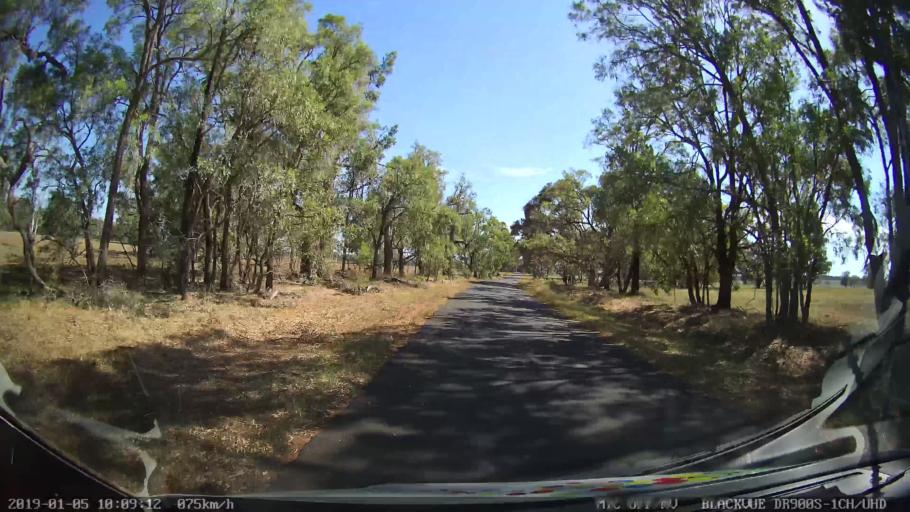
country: AU
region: New South Wales
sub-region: Gilgandra
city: Gilgandra
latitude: -31.6336
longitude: 148.8850
